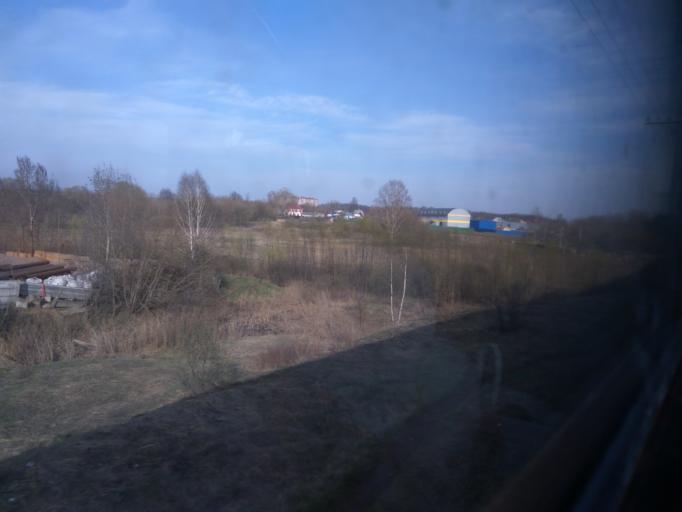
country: RU
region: Moskovskaya
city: Ramenskoye
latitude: 55.5433
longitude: 38.2874
